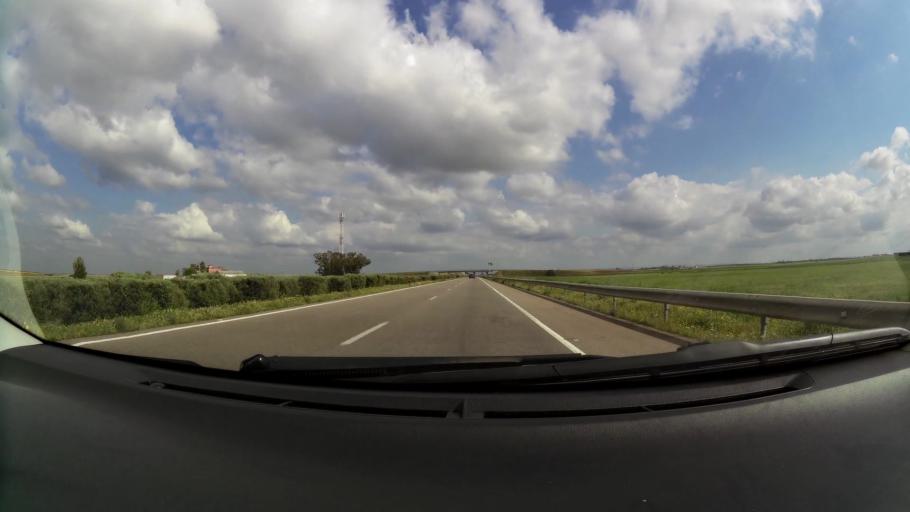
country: MA
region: Chaouia-Ouardigha
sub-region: Settat Province
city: Berrechid
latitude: 33.2931
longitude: -7.5529
